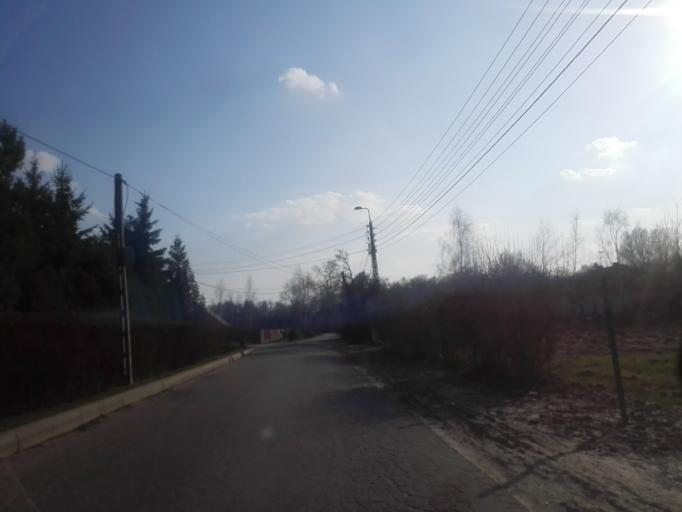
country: PL
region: Masovian Voivodeship
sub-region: Powiat piaseczynski
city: Konstancin-Jeziorna
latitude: 52.1401
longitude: 21.1425
